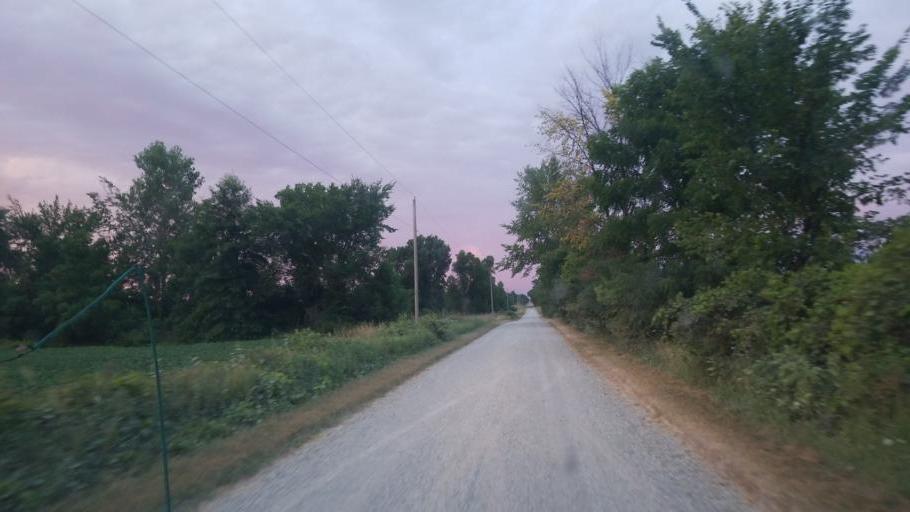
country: US
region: Ohio
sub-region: Defiance County
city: Hicksville
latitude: 41.3450
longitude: -84.8041
